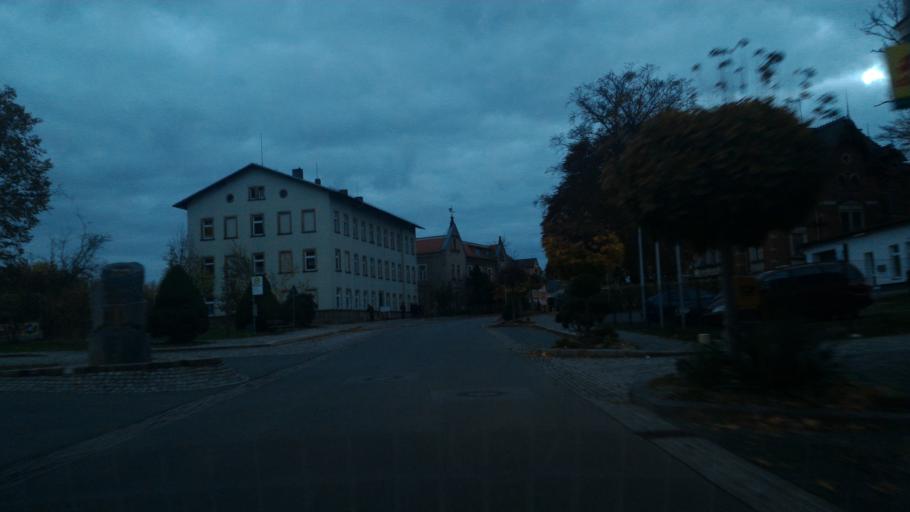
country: DE
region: Saxony
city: Ebersbach
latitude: 51.0047
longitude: 14.5779
